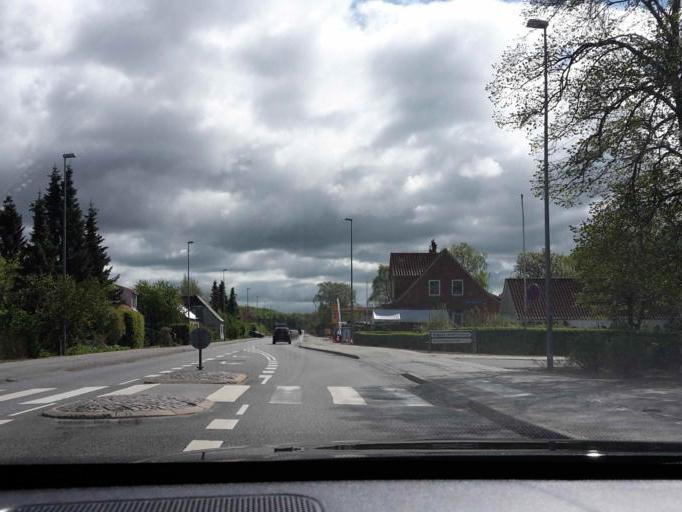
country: DK
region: Central Jutland
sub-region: Norddjurs Kommune
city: Auning
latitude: 56.4293
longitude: 10.3833
